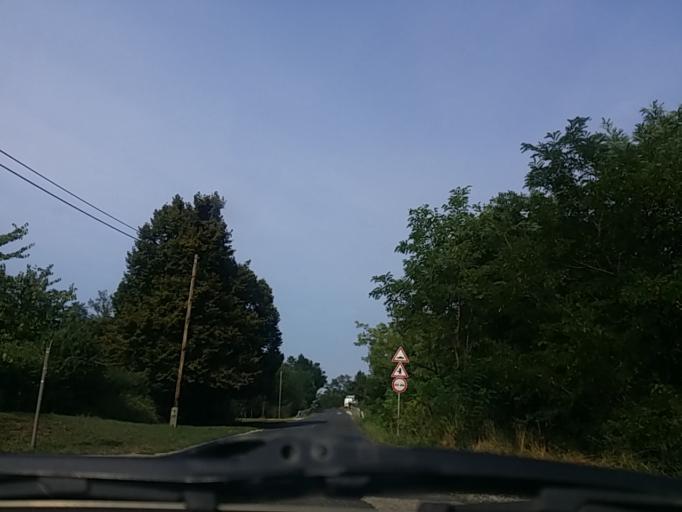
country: HU
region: Komarom-Esztergom
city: Kornye
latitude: 47.5248
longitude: 18.3714
